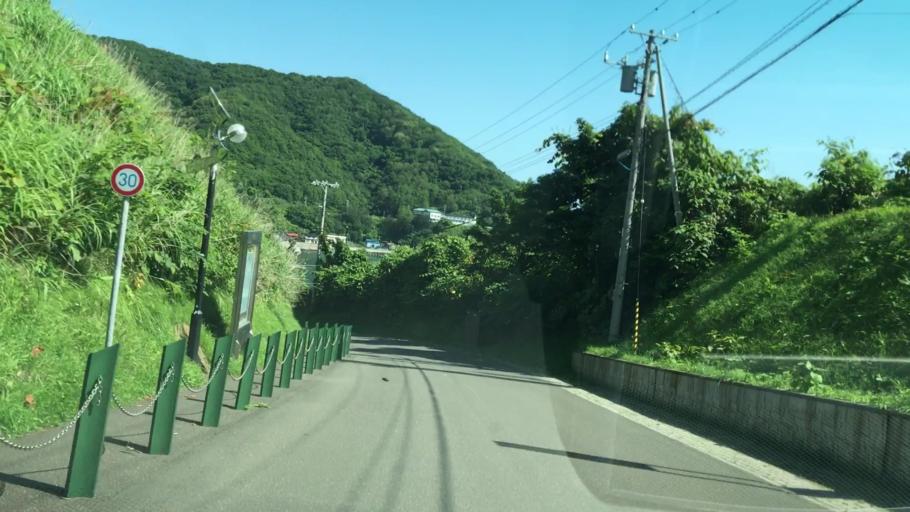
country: JP
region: Hokkaido
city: Iwanai
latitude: 43.1439
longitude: 140.4256
